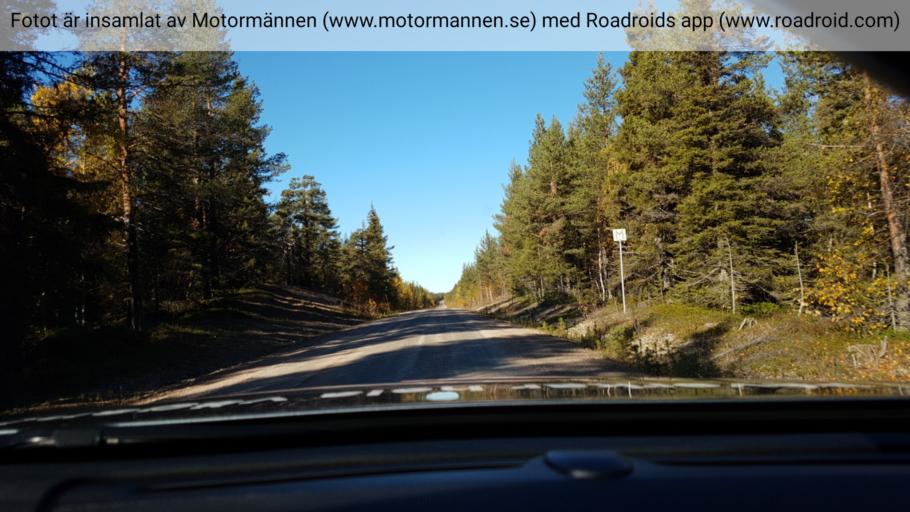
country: SE
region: Norrbotten
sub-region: Gallivare Kommun
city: Gaellivare
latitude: 66.6690
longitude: 20.9352
